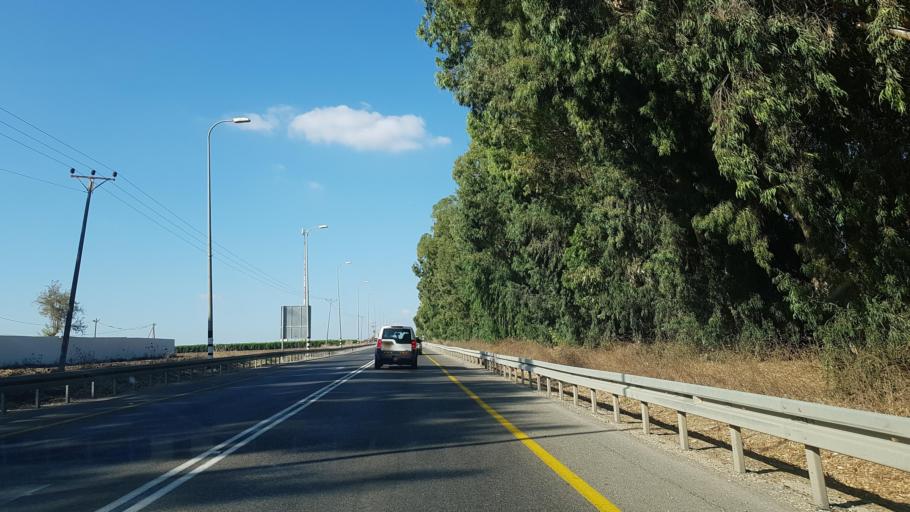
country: PS
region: West Bank
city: Tulkarm
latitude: 32.3158
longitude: 34.9992
